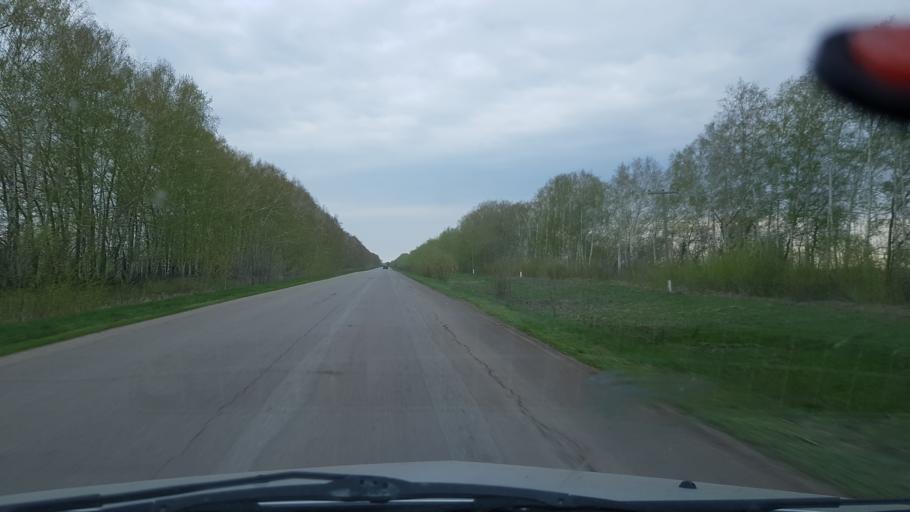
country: RU
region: Samara
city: Podstepki
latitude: 53.6620
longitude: 49.2046
